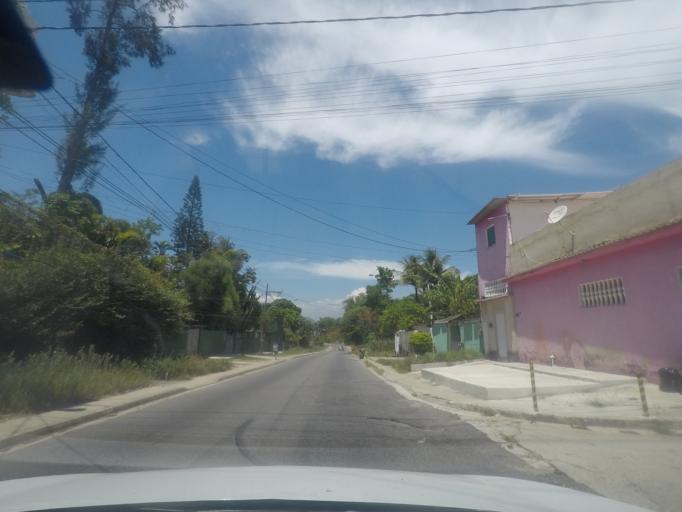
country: BR
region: Rio de Janeiro
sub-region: Itaguai
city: Itaguai
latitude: -22.9810
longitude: -43.6838
